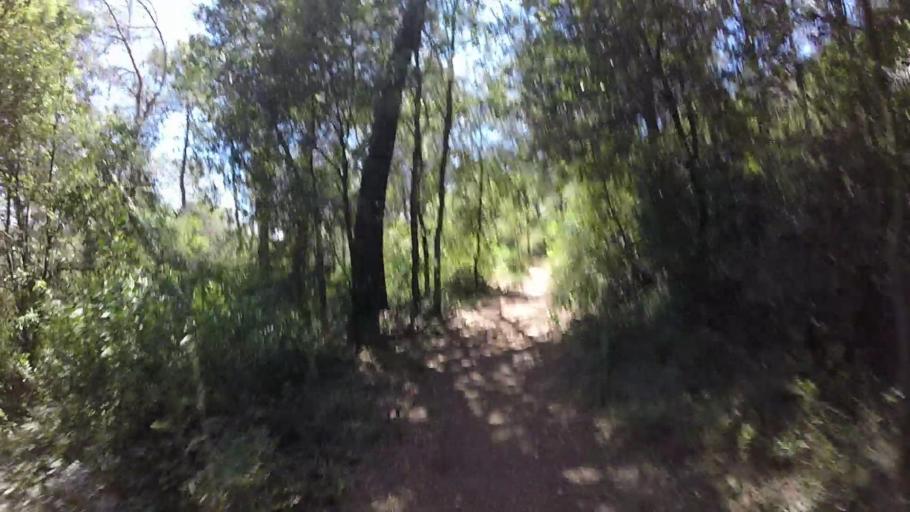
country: FR
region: Provence-Alpes-Cote d'Azur
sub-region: Departement des Alpes-Maritimes
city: Vallauris
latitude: 43.6124
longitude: 7.0471
